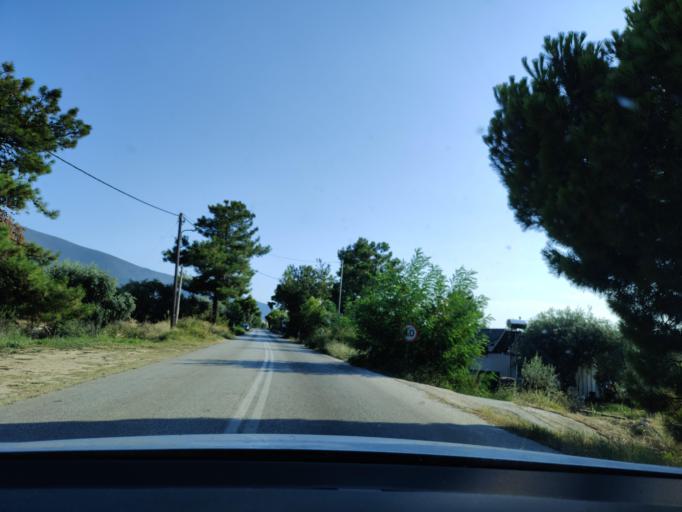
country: GR
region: East Macedonia and Thrace
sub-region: Nomos Kavalas
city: Prinos
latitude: 40.7138
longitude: 24.5347
